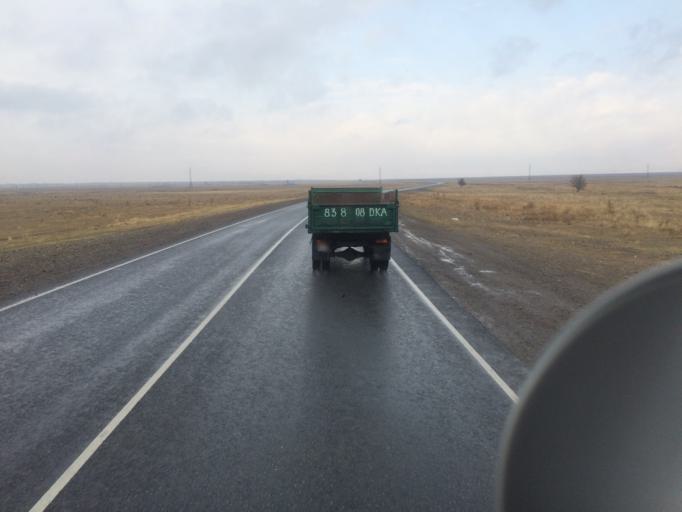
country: KZ
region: Zhambyl
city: Georgiyevka
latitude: 43.0437
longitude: 74.7570
